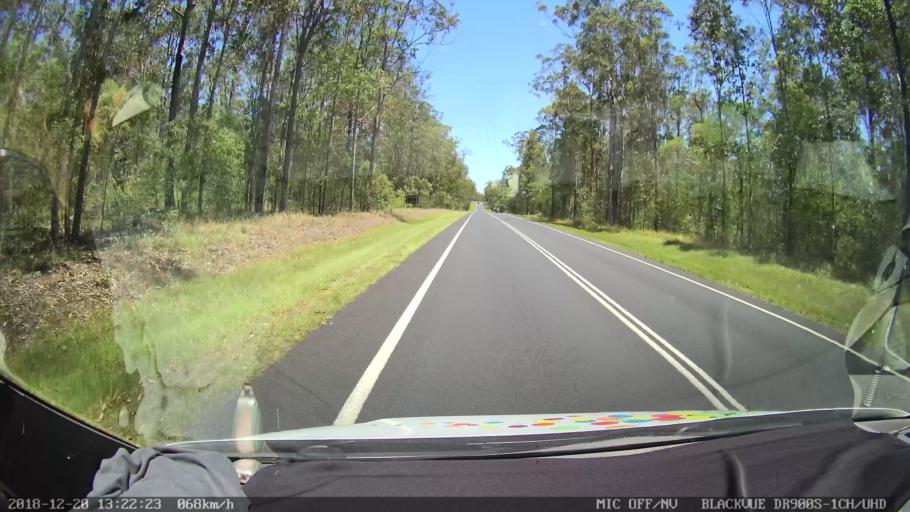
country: AU
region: New South Wales
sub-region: Richmond Valley
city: Casino
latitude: -29.0913
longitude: 153.0015
